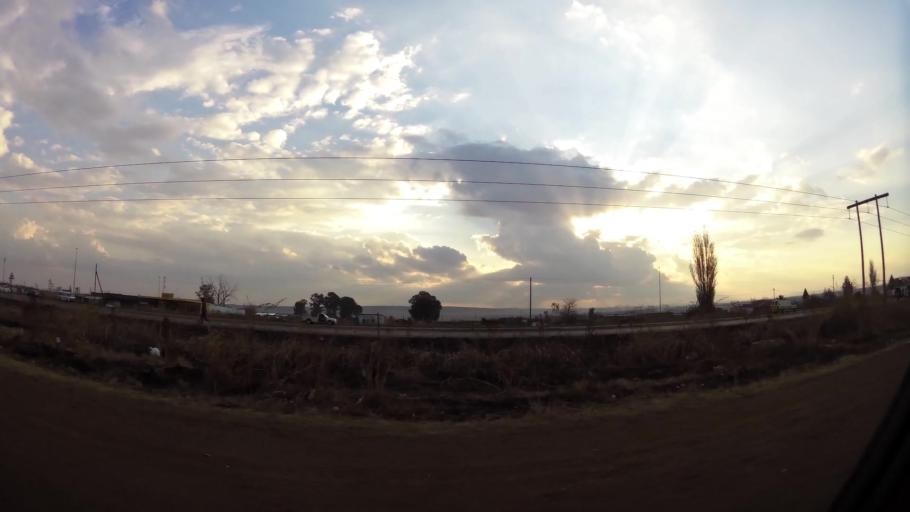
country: ZA
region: Gauteng
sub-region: City of Johannesburg Metropolitan Municipality
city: Orange Farm
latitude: -26.5553
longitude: 27.8303
